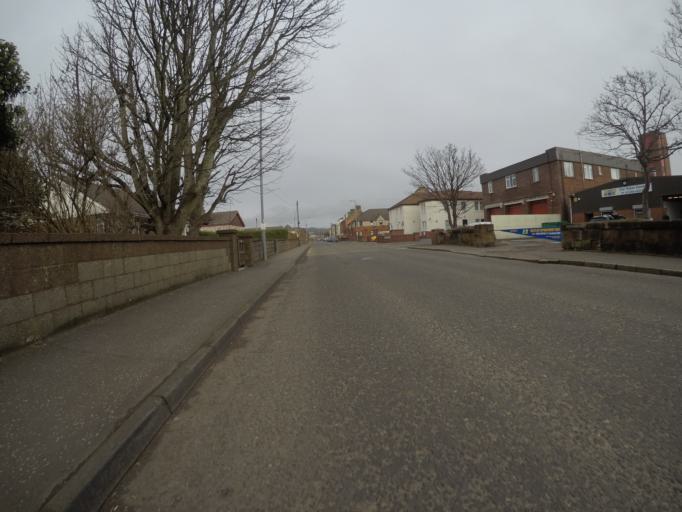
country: GB
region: Scotland
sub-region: North Ayrshire
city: Ardrossan
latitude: 55.6433
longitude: -4.8141
